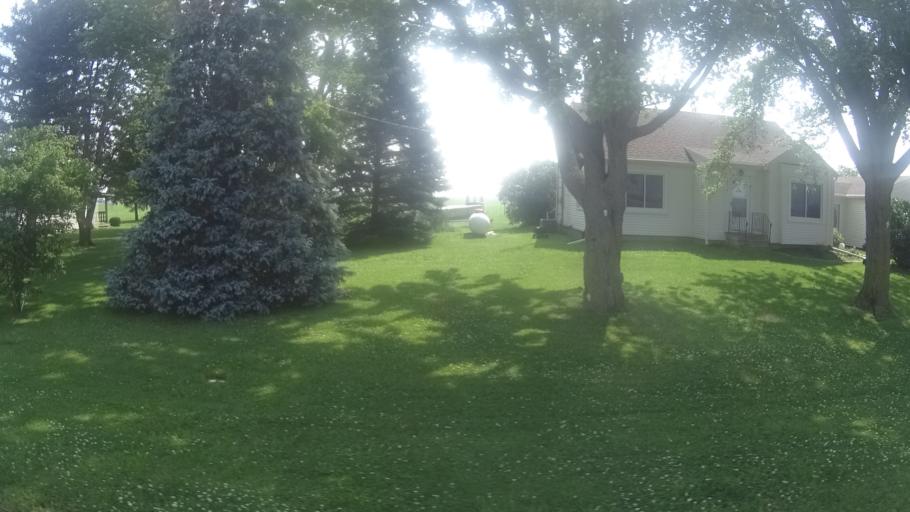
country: US
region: Ohio
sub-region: Huron County
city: Monroeville
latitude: 41.3250
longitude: -82.7183
